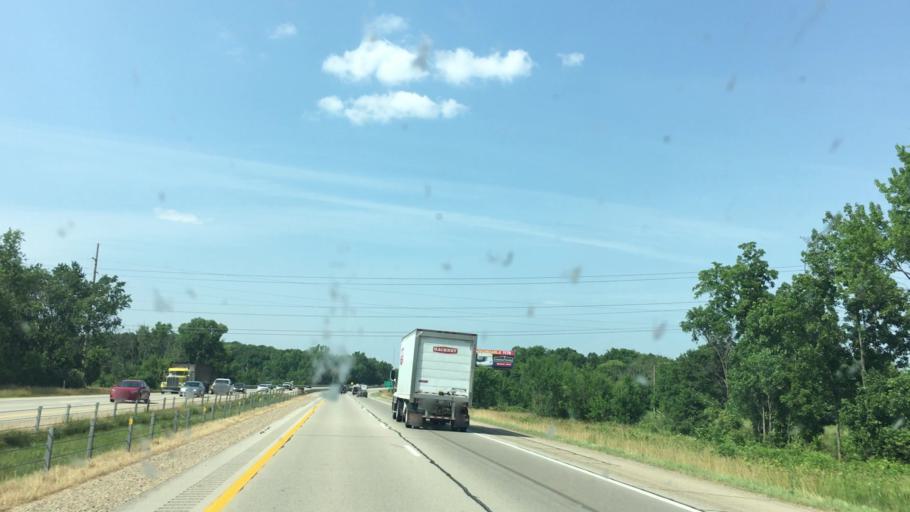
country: US
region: Michigan
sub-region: Kent County
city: Byron Center
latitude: 42.7579
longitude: -85.6736
